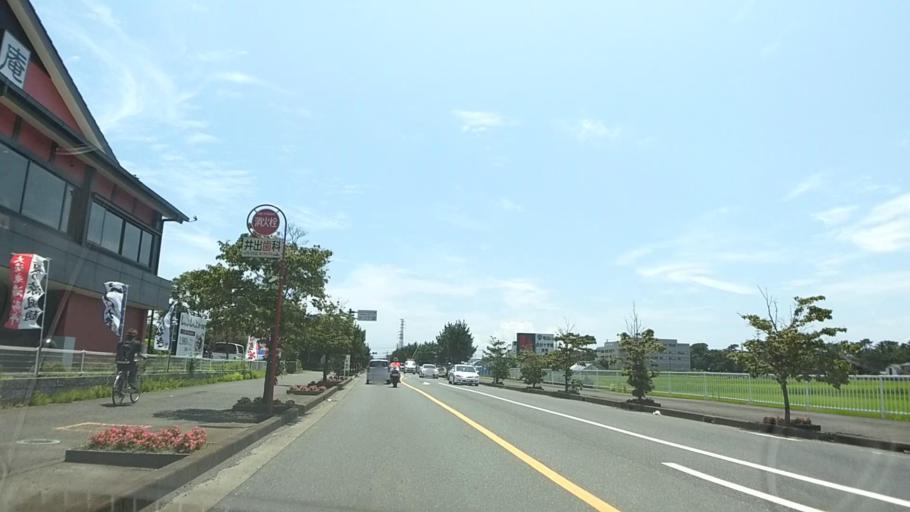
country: JP
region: Kanagawa
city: Chigasaki
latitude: 35.3765
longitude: 139.3844
